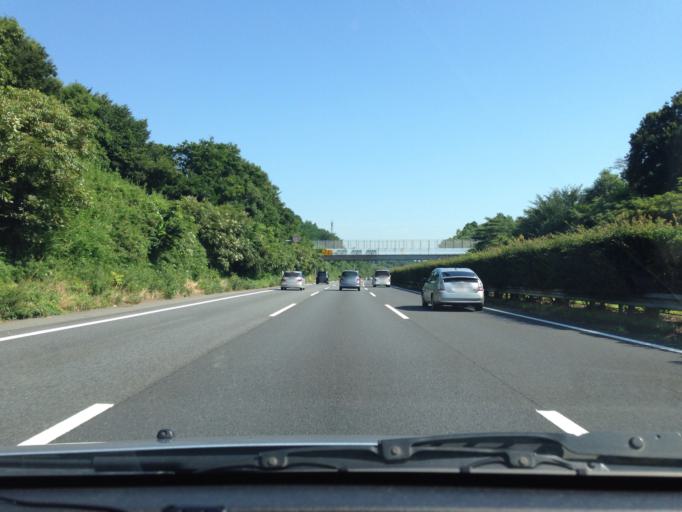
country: JP
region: Ibaraki
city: Naka
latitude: 36.0757
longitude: 140.1549
